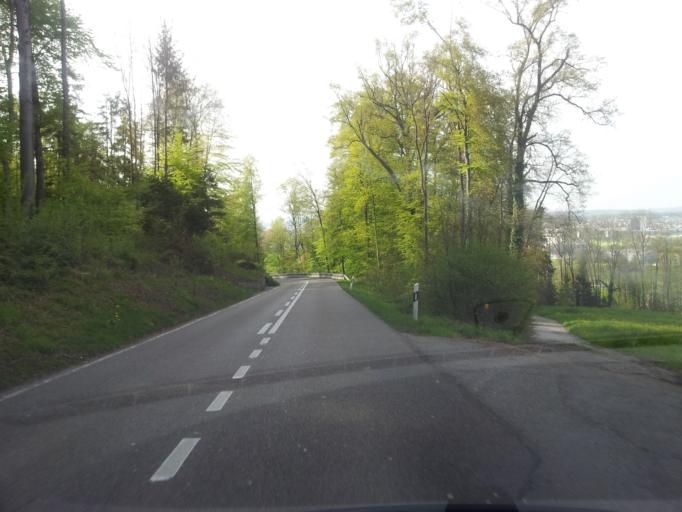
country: CH
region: Zurich
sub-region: Bezirk Uster
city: Gockhausen
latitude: 47.3872
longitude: 8.5985
